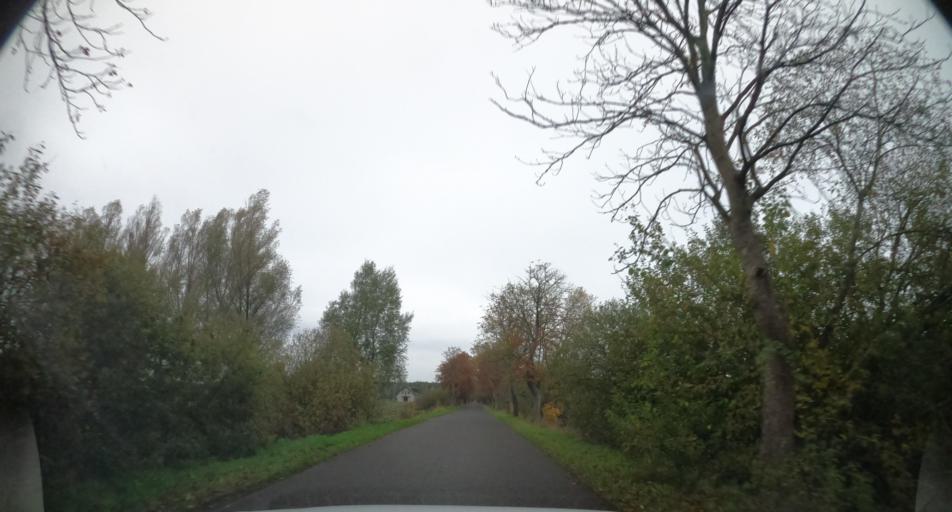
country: PL
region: West Pomeranian Voivodeship
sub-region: Powiat kamienski
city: Wolin
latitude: 53.9321
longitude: 14.6089
